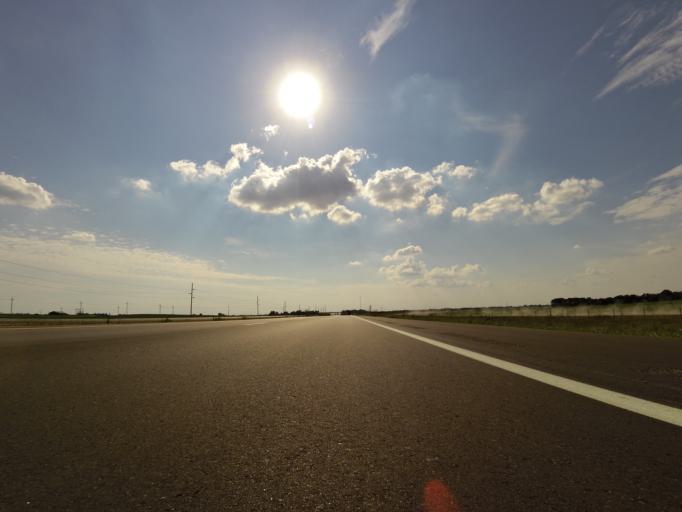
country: US
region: Kansas
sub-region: Reno County
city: South Hutchinson
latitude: 38.0133
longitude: -97.9536
